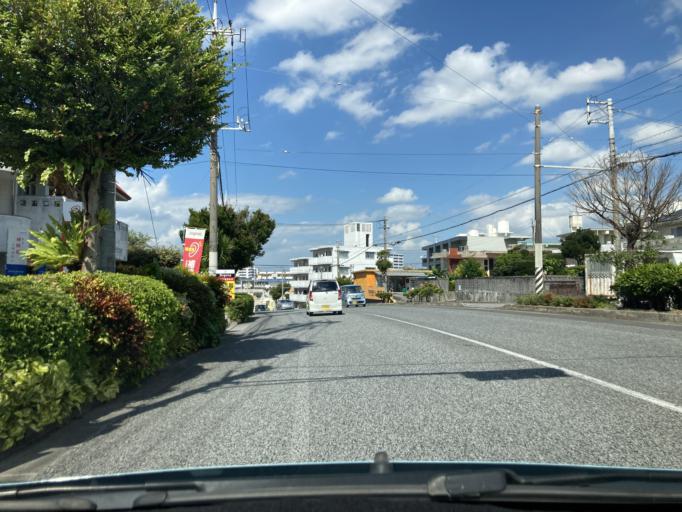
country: JP
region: Okinawa
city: Ginowan
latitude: 26.2507
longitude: 127.7576
